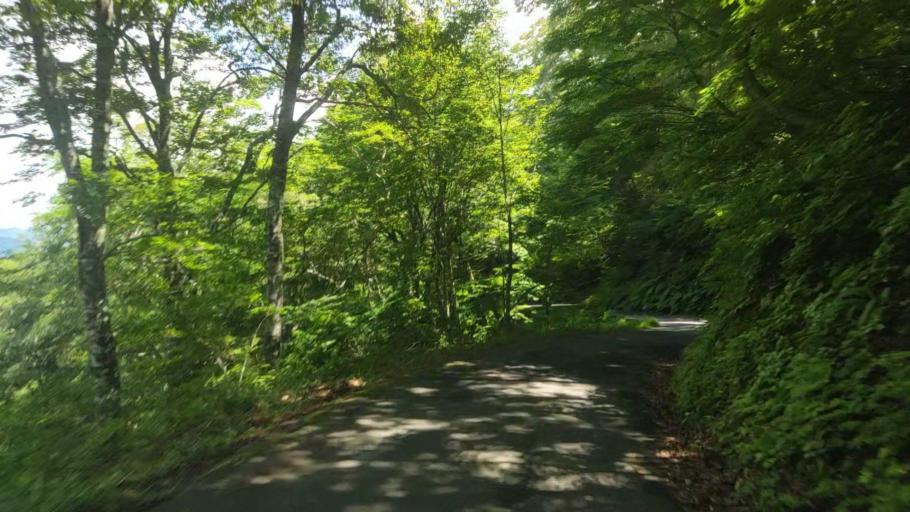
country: JP
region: Fukui
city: Ono
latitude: 35.7689
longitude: 136.5360
